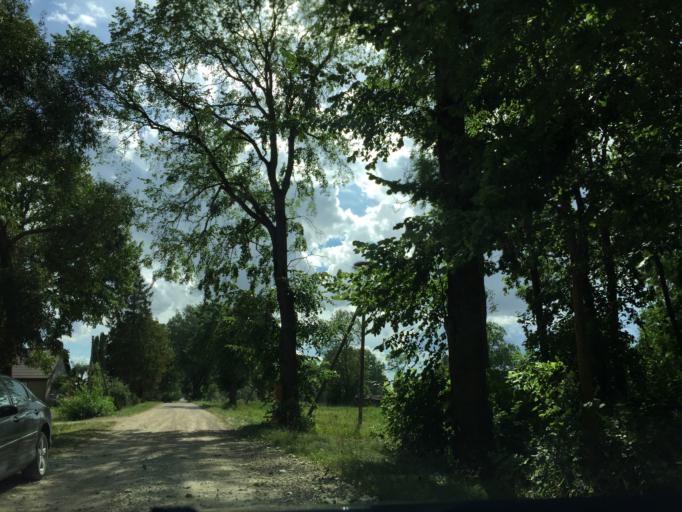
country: LT
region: Siauliu apskritis
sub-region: Joniskis
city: Joniskis
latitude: 56.3465
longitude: 23.6235
